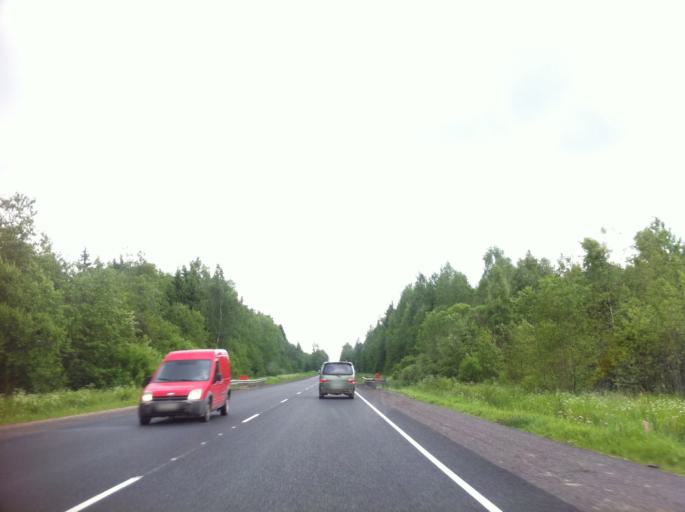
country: RU
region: Leningrad
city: Rozhdestveno
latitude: 59.1836
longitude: 29.9187
